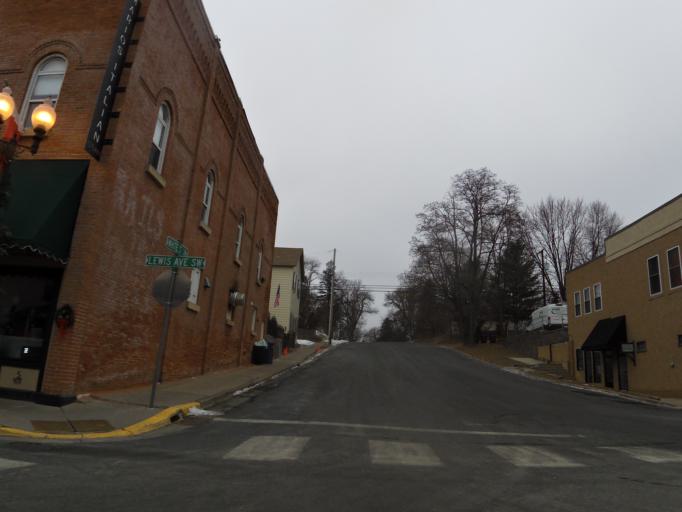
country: US
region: Minnesota
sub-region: Carver County
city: Watertown
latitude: 44.9628
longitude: -93.8480
